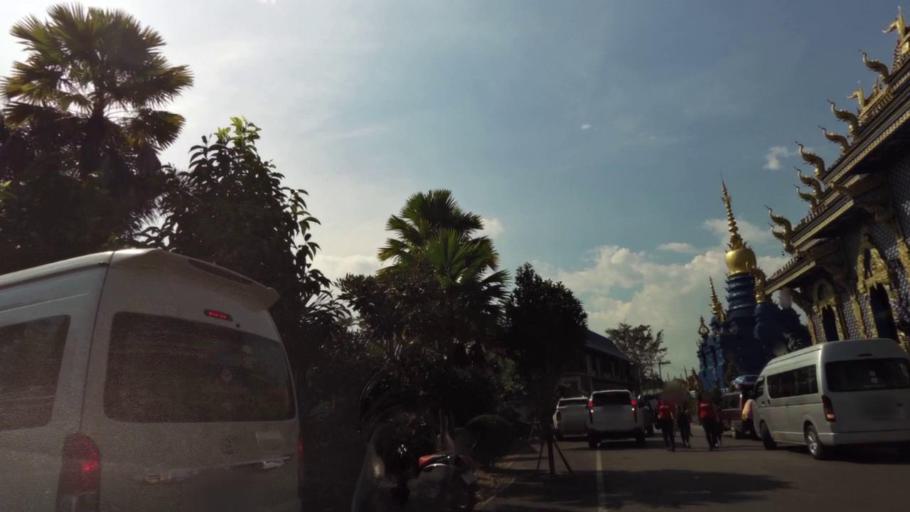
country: TH
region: Chiang Rai
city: Chiang Rai
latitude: 19.9233
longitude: 99.8419
